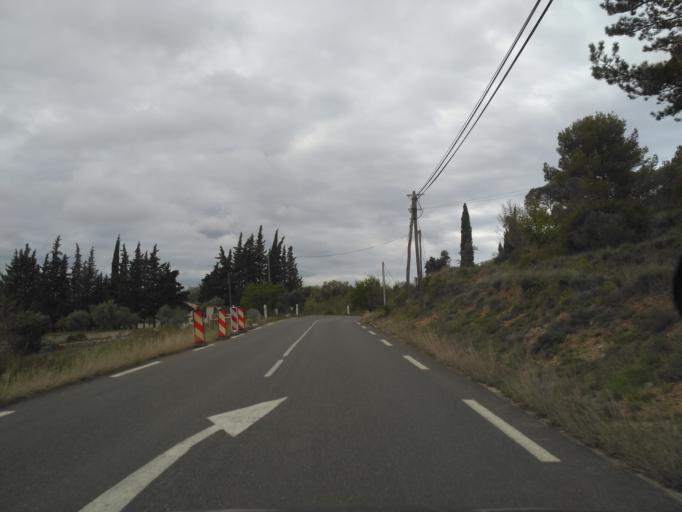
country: FR
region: Provence-Alpes-Cote d'Azur
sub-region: Departement du Var
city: Saint-Julien
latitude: 43.6304
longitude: 5.9410
